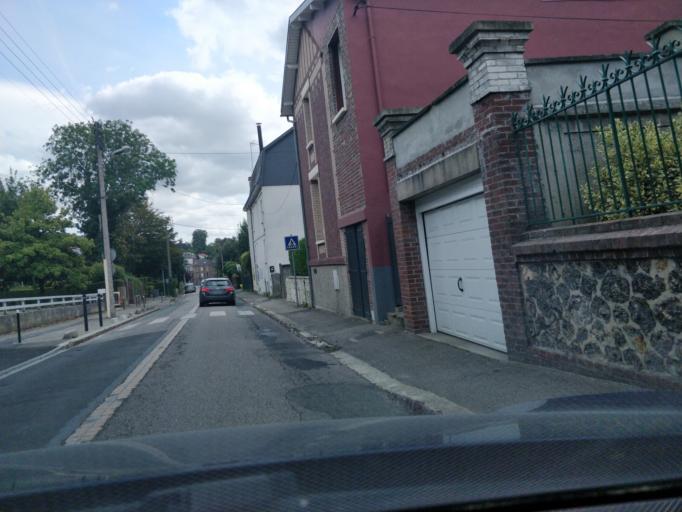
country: FR
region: Haute-Normandie
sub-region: Departement de la Seine-Maritime
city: Mont-Saint-Aignan
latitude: 49.4590
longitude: 1.0935
